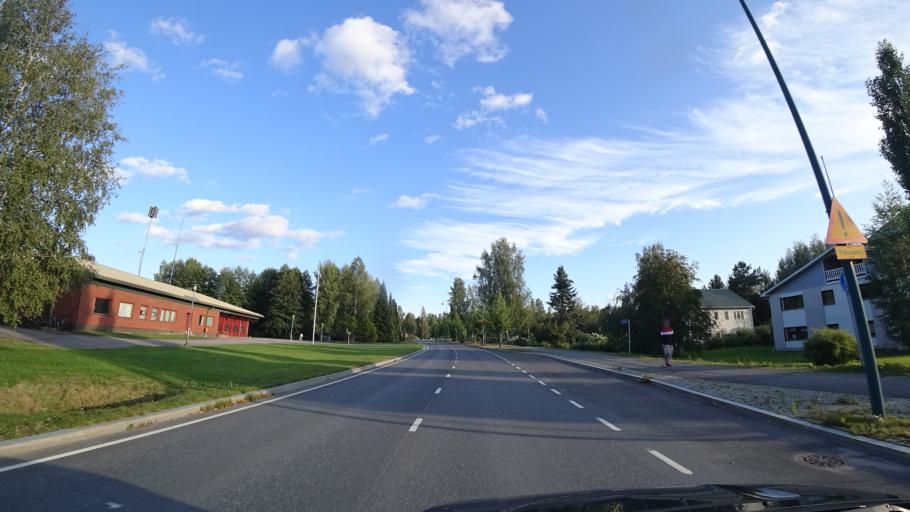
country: FI
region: Haeme
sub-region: Haemeenlinna
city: Lammi
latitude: 61.0748
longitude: 25.0114
